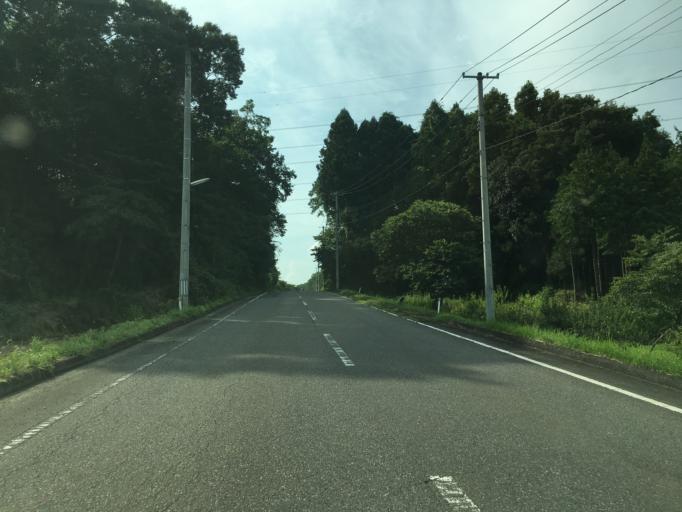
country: JP
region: Fukushima
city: Sukagawa
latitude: 37.3282
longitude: 140.4332
